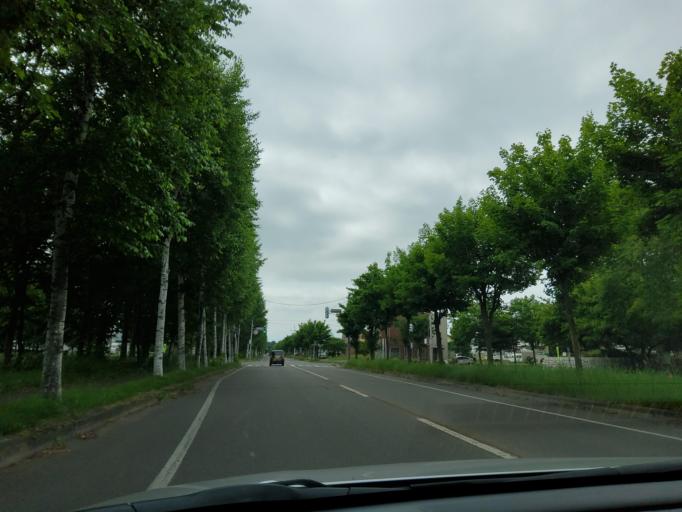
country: JP
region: Hokkaido
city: Obihiro
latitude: 42.9121
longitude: 143.1373
